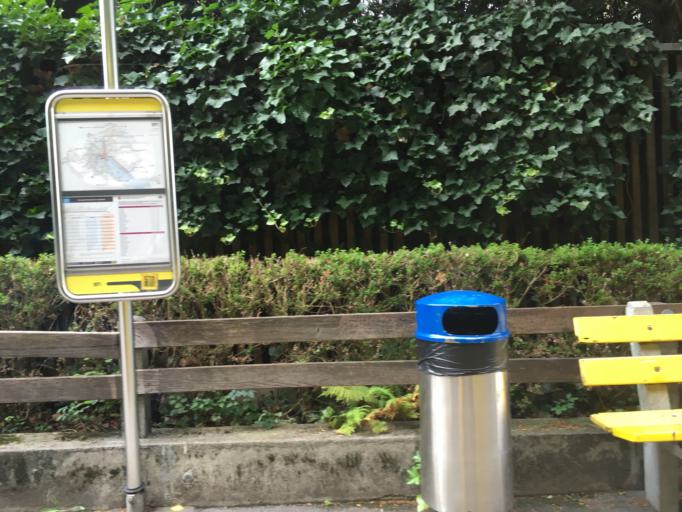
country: CH
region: Bern
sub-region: Thun District
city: Thun
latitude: 46.7474
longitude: 7.6399
